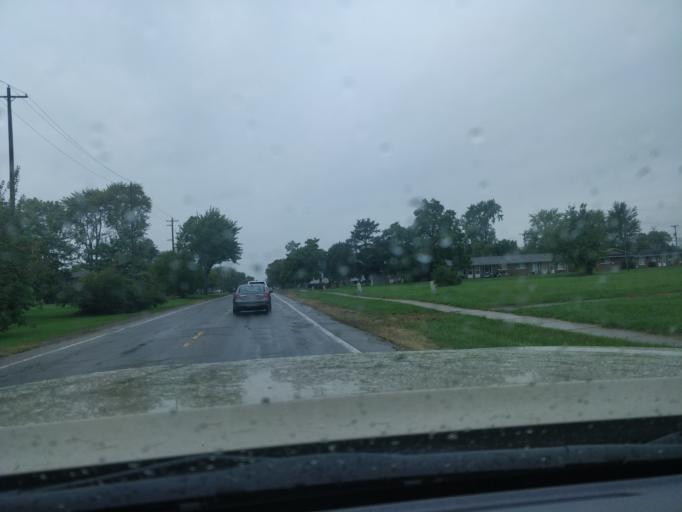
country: US
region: Michigan
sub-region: Wayne County
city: Woodhaven
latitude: 42.1266
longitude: -83.2119
